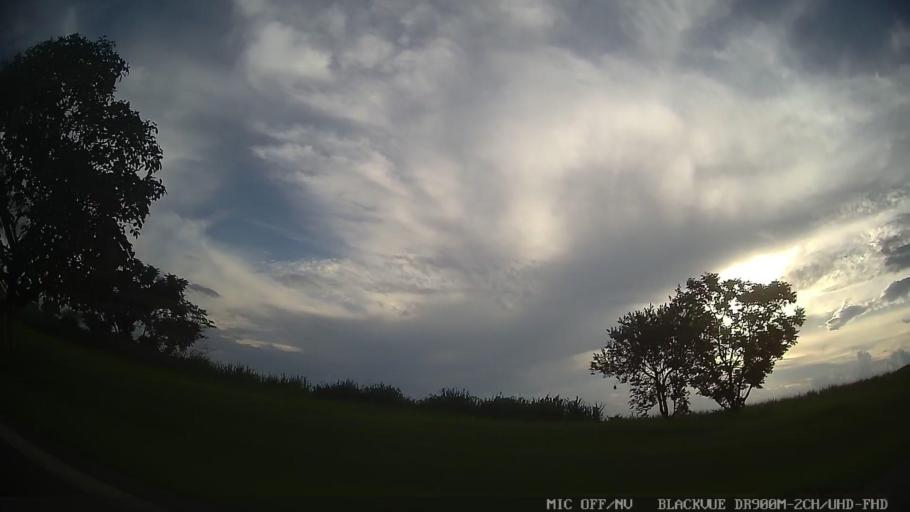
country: BR
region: Sao Paulo
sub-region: Porto Feliz
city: Porto Feliz
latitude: -23.2030
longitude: -47.6030
